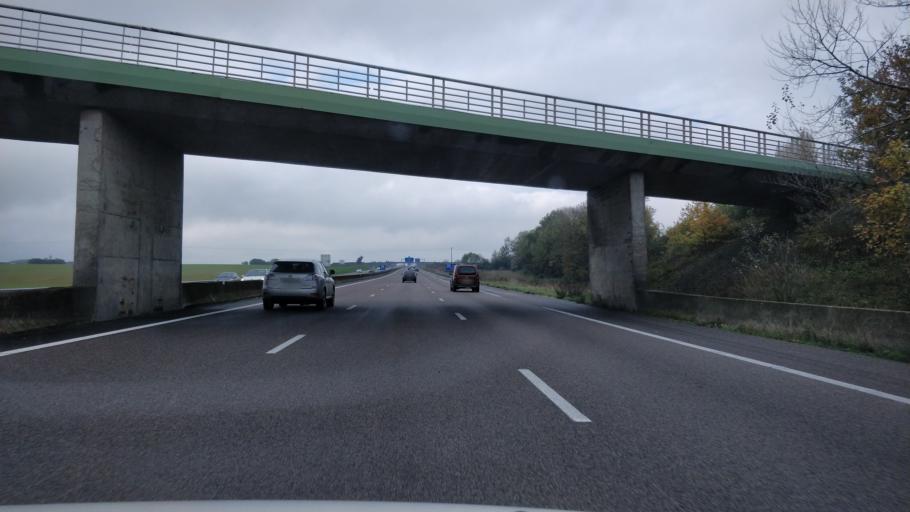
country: FR
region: Haute-Normandie
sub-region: Departement de l'Eure
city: Bourg-Achard
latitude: 49.3632
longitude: 0.8457
